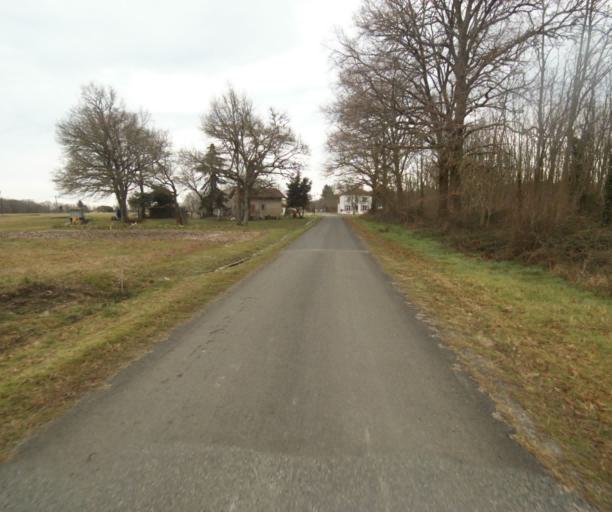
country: FR
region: Aquitaine
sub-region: Departement des Landes
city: Gabarret
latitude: 44.0095
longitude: -0.0236
